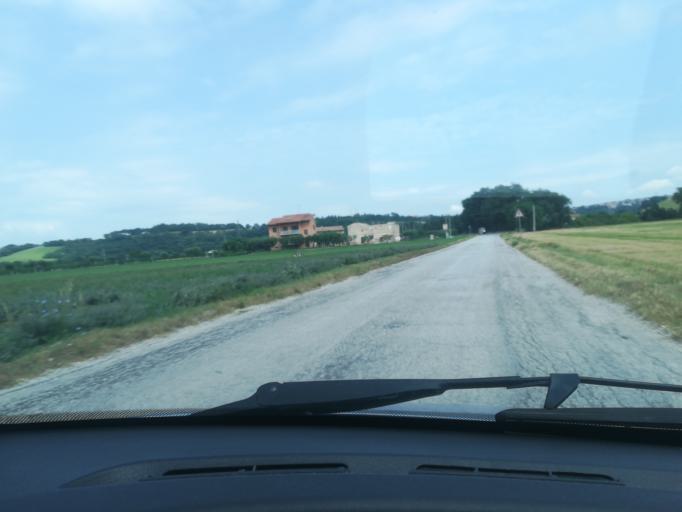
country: IT
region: The Marches
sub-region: Provincia di Macerata
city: Sforzacosta
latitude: 43.2672
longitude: 13.4387
